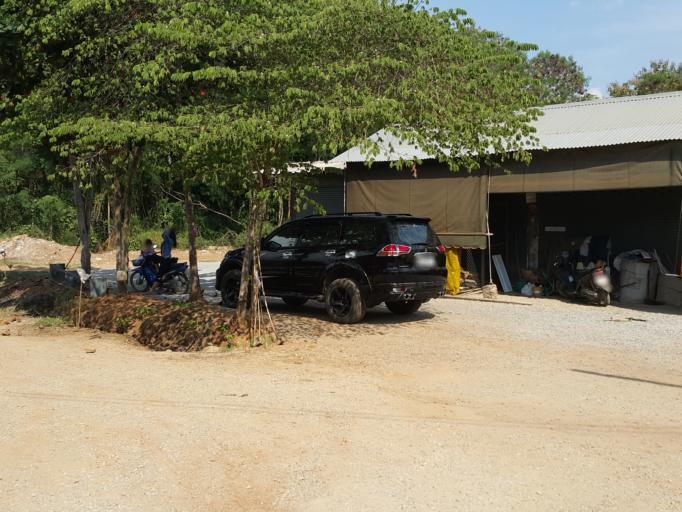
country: TH
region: Sukhothai
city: Thung Saliam
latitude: 17.3184
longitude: 99.5533
